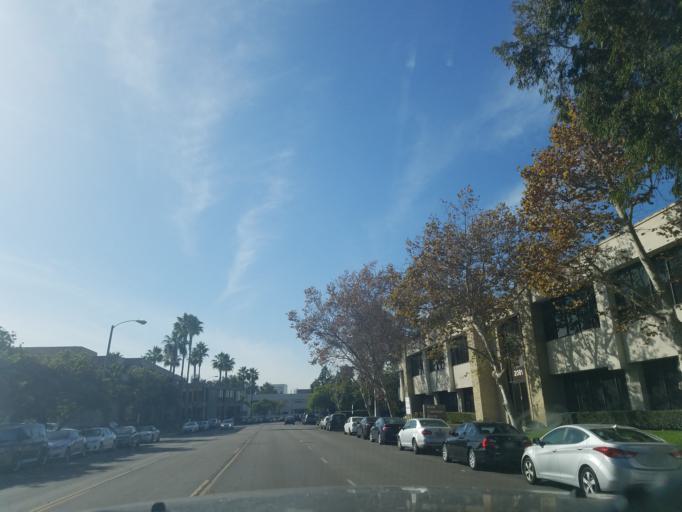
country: US
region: California
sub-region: Orange County
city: Irvine
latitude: 33.6797
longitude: -117.8560
